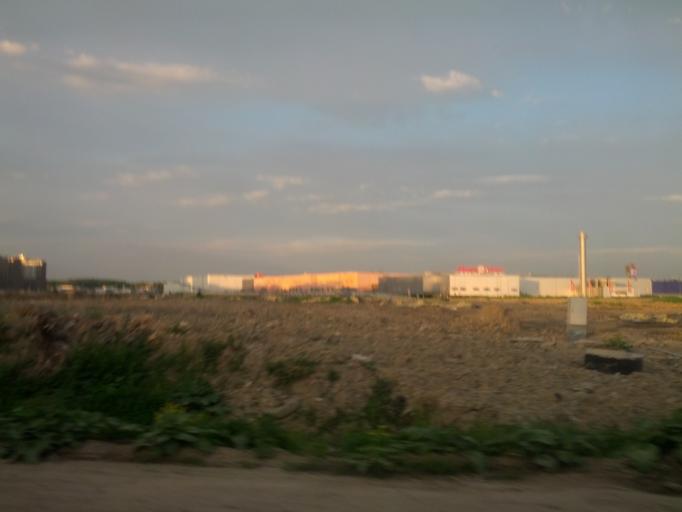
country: RU
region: Leningrad
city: Rybatskoye
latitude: 59.8948
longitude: 30.5044
